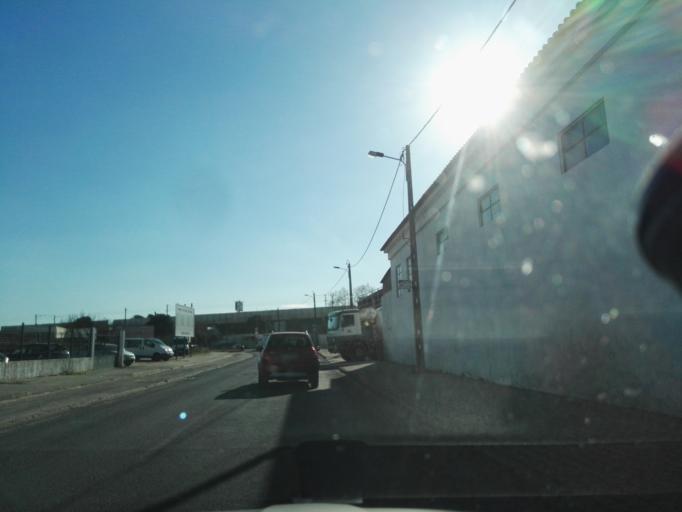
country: PT
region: Setubal
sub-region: Seixal
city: Corroios
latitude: 38.6337
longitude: -9.1442
